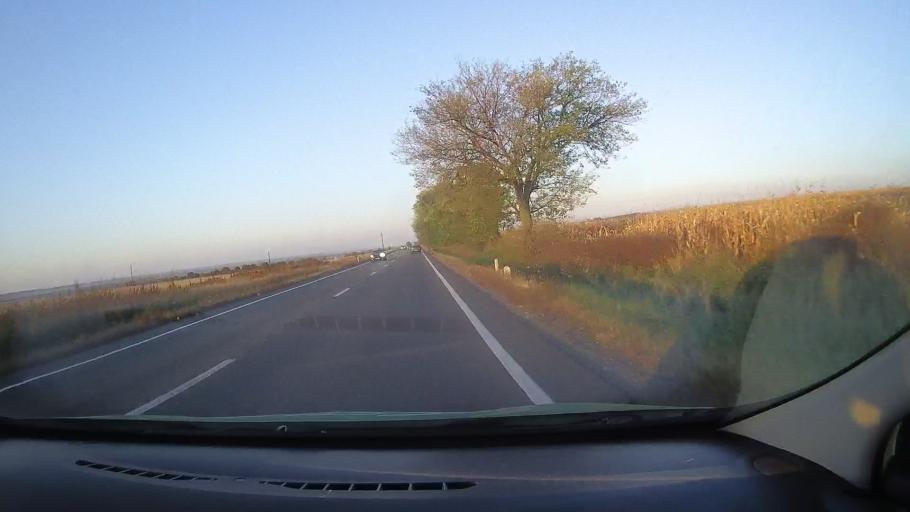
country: RO
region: Bihor
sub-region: Comuna Rosiori
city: Rosiori
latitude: 47.2706
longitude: 21.9755
